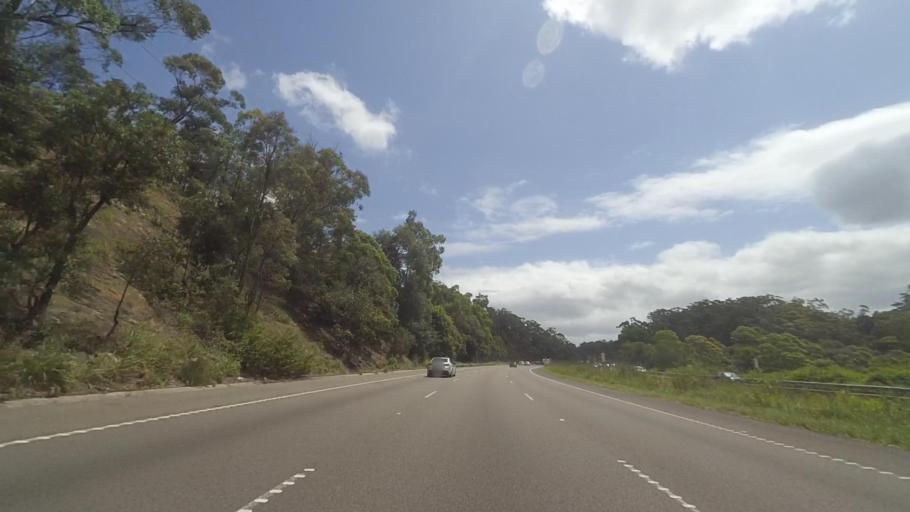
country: AU
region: New South Wales
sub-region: Gosford Shire
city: Lisarow
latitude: -33.3552
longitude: 151.3539
